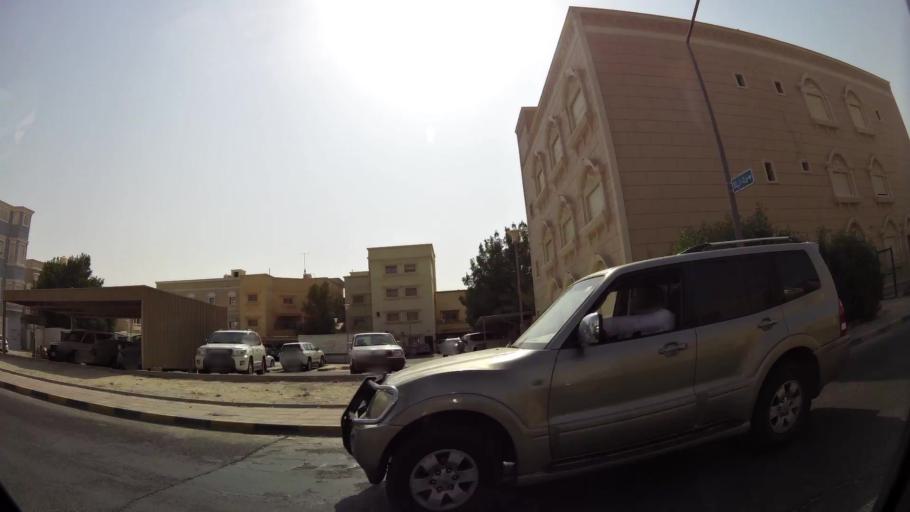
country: KW
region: Muhafazat al Jahra'
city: Al Jahra'
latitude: 29.3246
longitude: 47.6670
